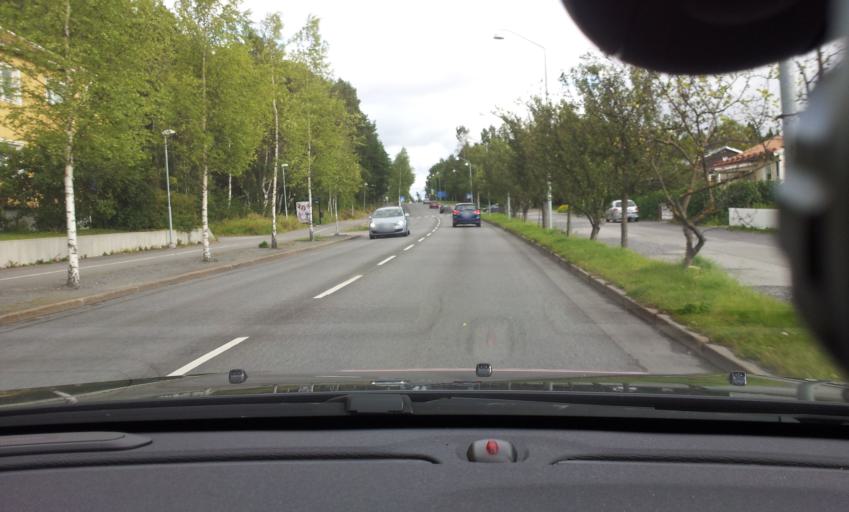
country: SE
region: Jaemtland
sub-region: OEstersunds Kommun
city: Ostersund
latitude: 63.1610
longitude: 14.6640
